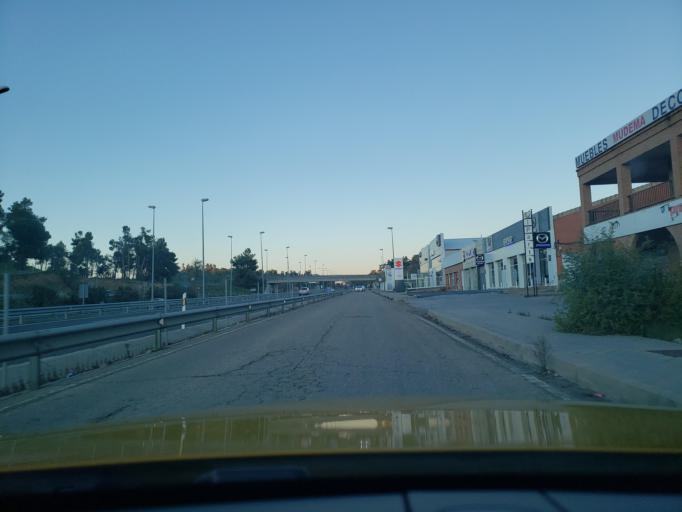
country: ES
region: Castille-La Mancha
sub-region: Province of Toledo
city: Bargas
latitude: 39.9157
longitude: -4.0072
